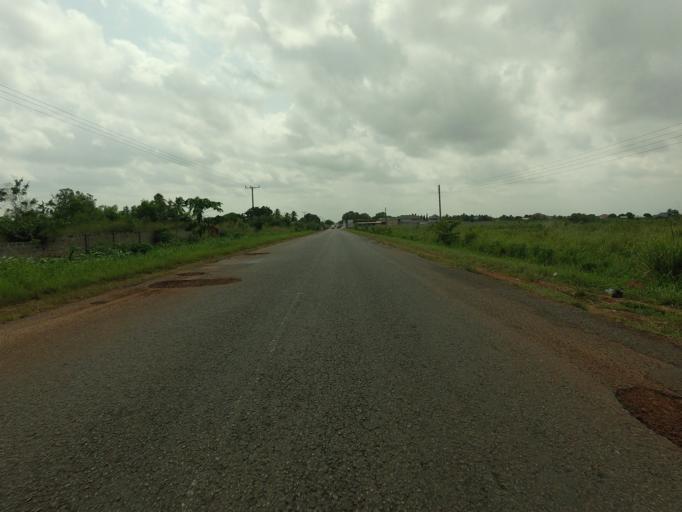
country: TG
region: Maritime
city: Lome
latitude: 6.1277
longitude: 1.1240
